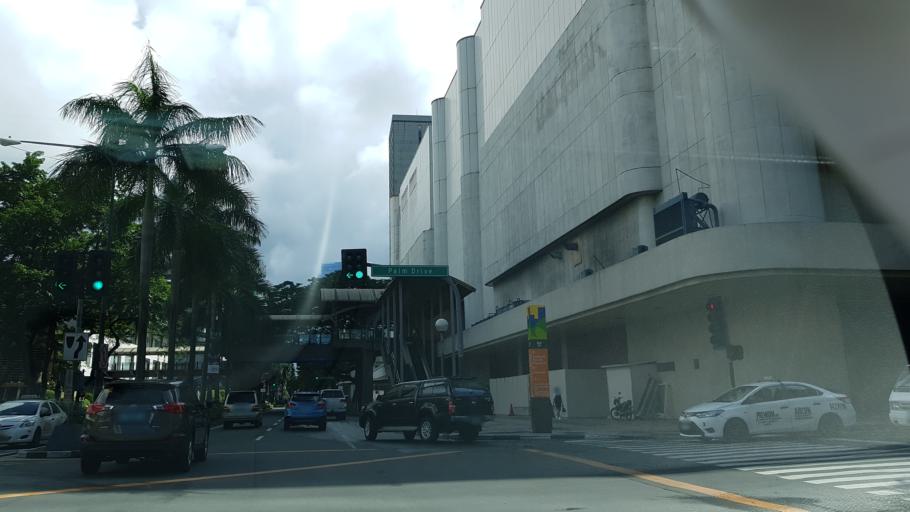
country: PH
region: Metro Manila
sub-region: Makati City
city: Makati City
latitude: 14.5515
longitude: 121.0231
